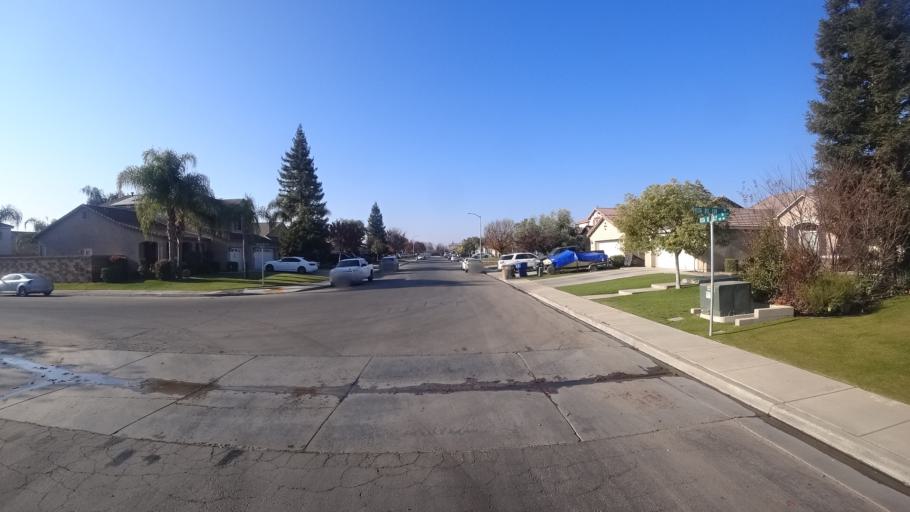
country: US
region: California
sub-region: Kern County
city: Greenacres
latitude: 35.3091
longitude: -119.1254
